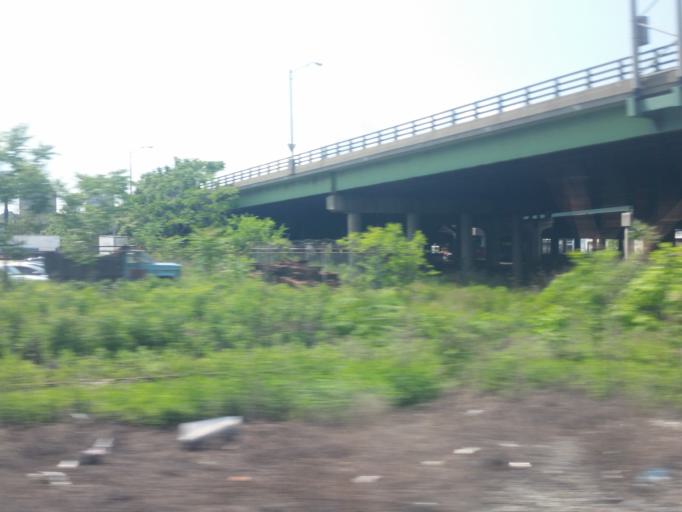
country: US
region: New Jersey
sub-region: Essex County
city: Newark
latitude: 40.7077
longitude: -74.1890
